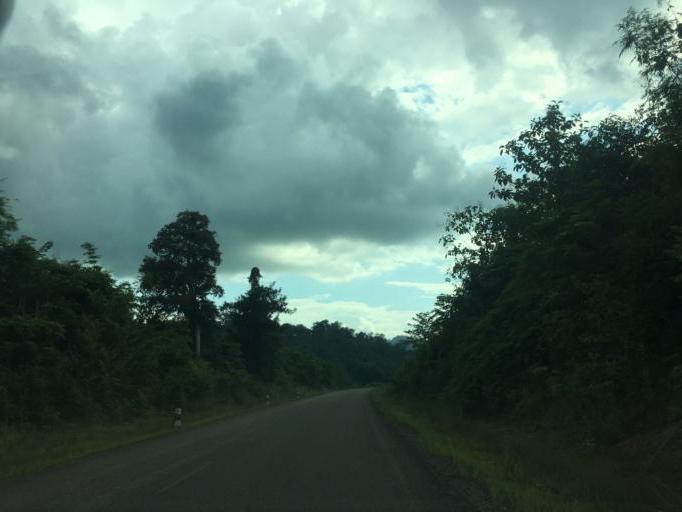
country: TH
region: Nong Khai
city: Sangkhom
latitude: 18.2015
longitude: 102.2247
